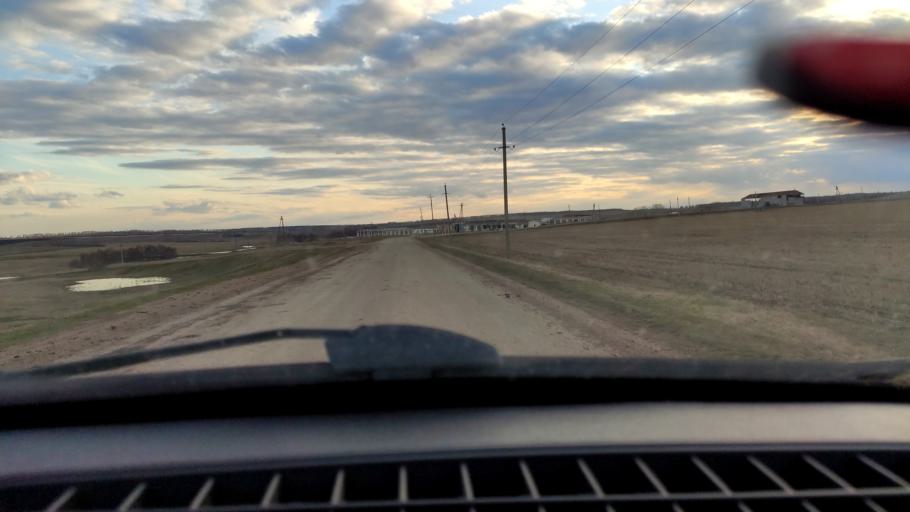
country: RU
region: Bashkortostan
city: Tolbazy
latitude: 53.9964
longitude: 55.6744
